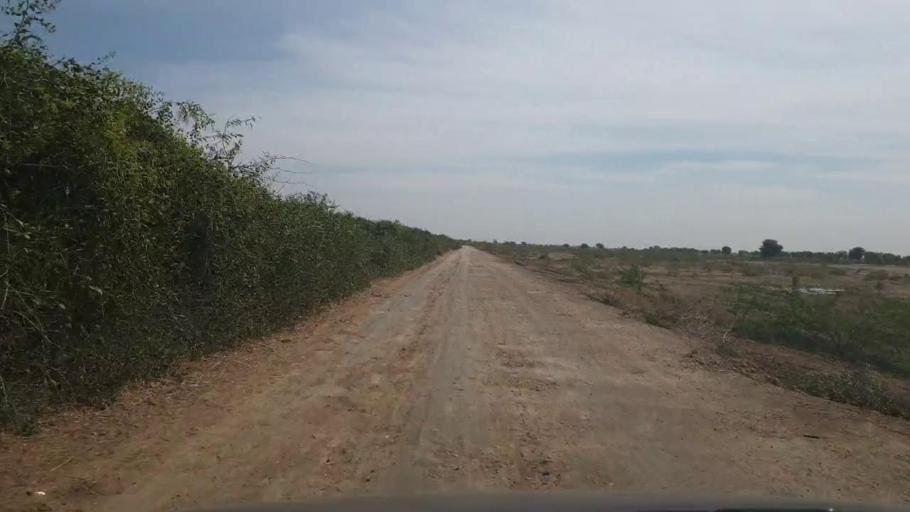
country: PK
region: Sindh
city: Kunri
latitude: 25.2934
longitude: 69.5837
